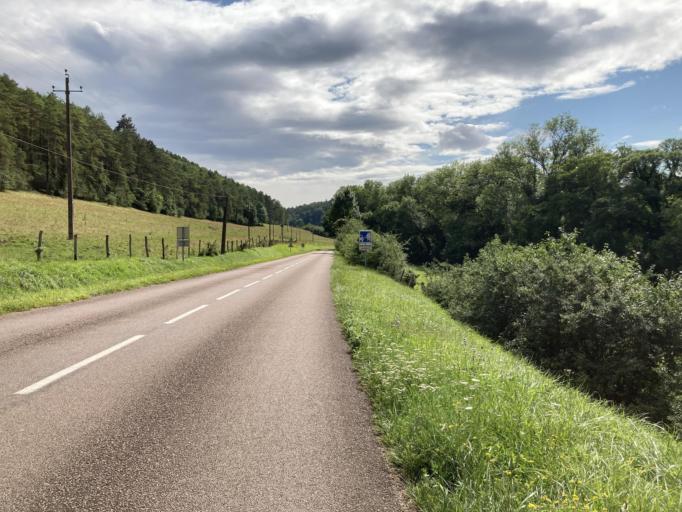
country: FR
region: Bourgogne
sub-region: Departement de la Cote-d'Or
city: Montbard
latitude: 47.6334
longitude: 4.3739
